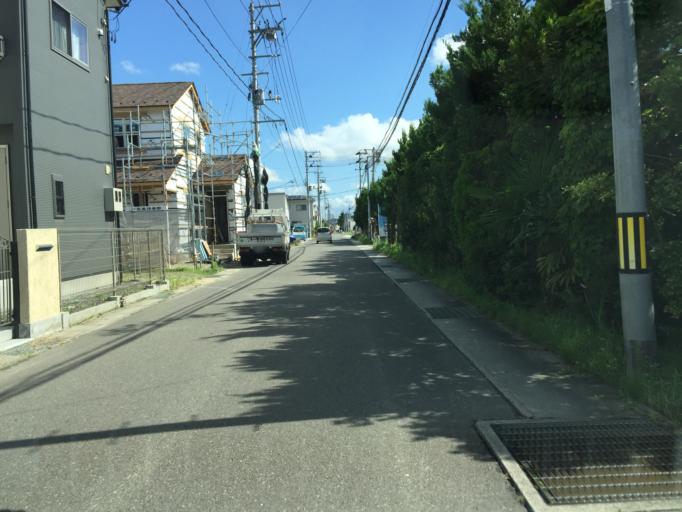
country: JP
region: Fukushima
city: Fukushima-shi
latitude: 37.7311
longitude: 140.4526
